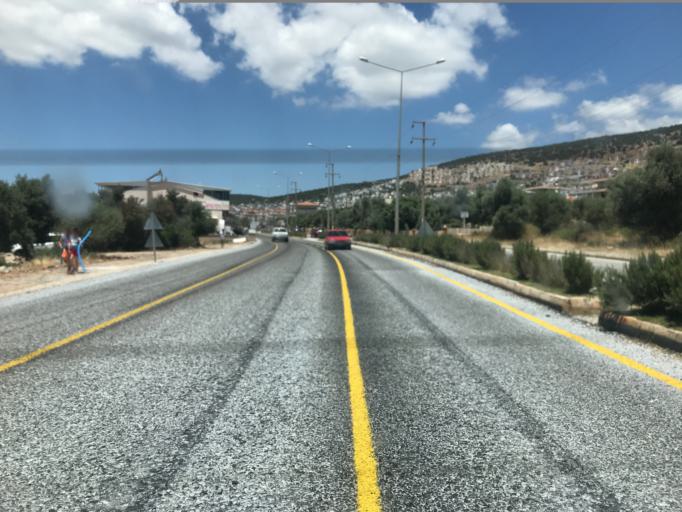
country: TR
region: Aydin
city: Sarikemer
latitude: 37.4147
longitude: 27.4207
